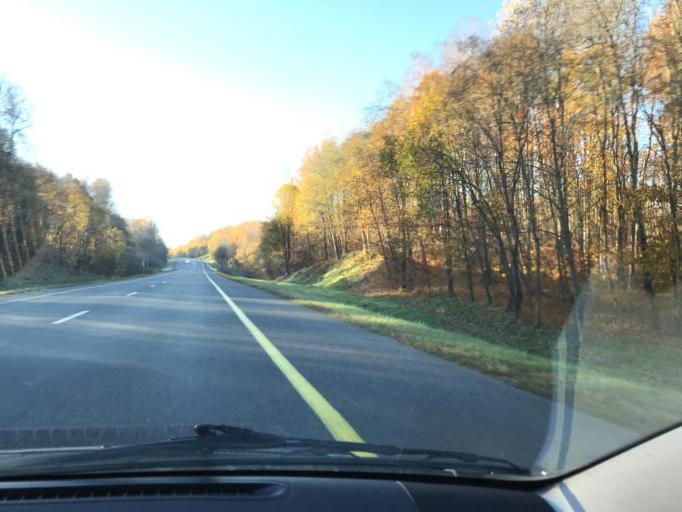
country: BY
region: Vitebsk
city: Vitebsk
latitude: 55.0289
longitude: 30.3234
